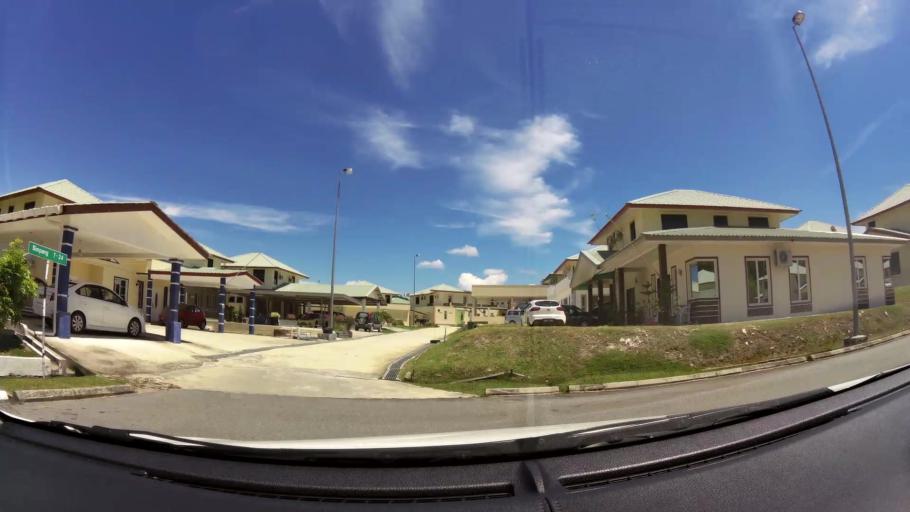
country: BN
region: Brunei and Muara
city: Bandar Seri Begawan
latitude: 5.0334
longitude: 115.0401
